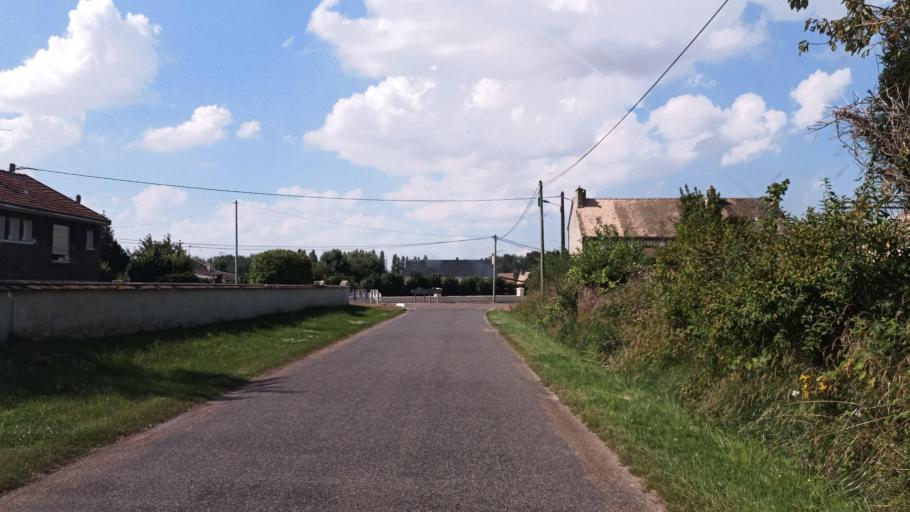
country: FR
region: Bourgogne
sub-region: Departement de l'Yonne
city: Saint-Valerien
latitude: 48.1443
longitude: 3.0897
